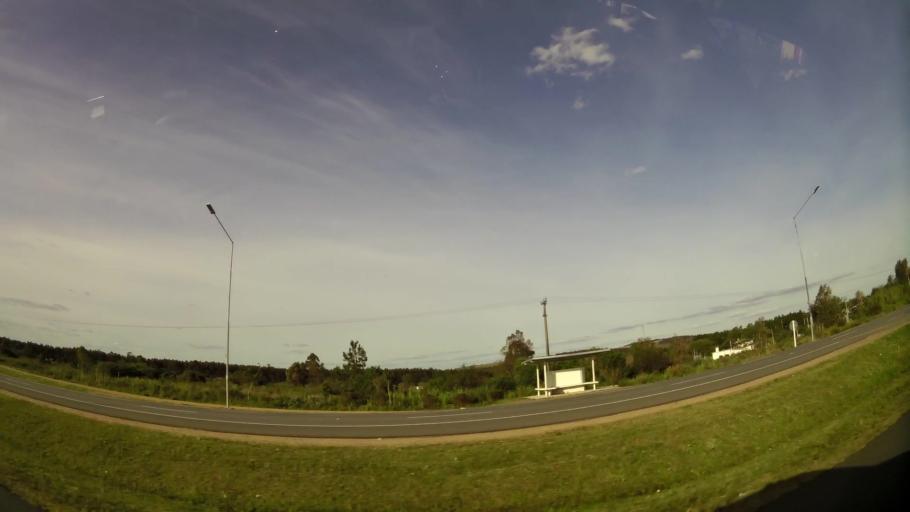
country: UY
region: Canelones
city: La Floresta
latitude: -34.7701
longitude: -55.5759
